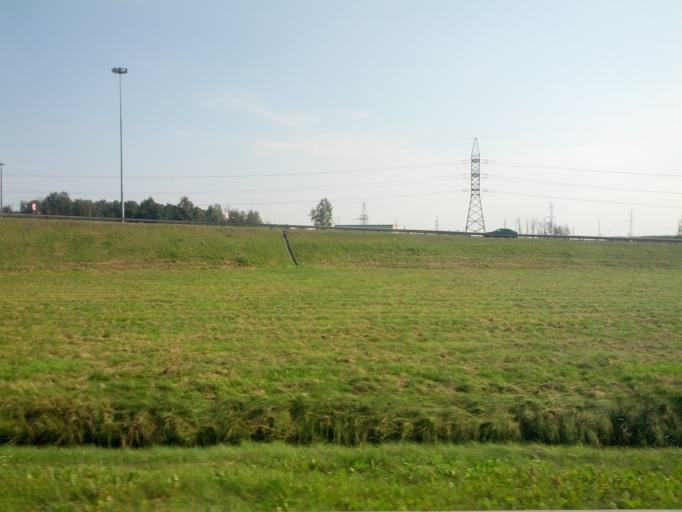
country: RU
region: Leningrad
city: Rybatskoye
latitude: 59.8905
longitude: 30.5177
